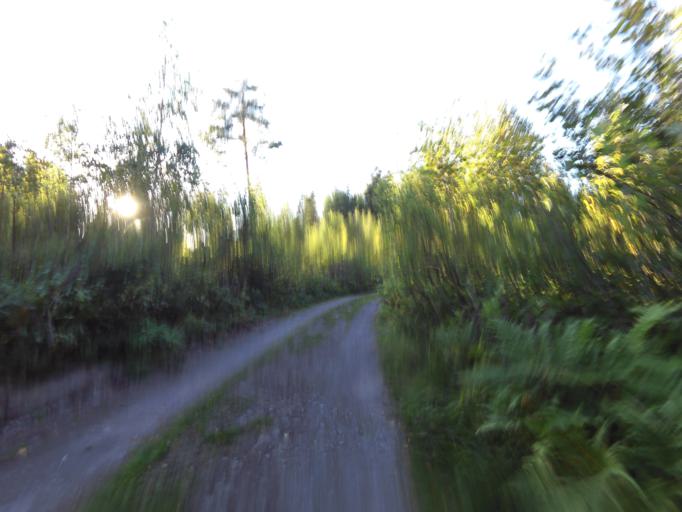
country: SE
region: Gaevleborg
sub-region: Gavle Kommun
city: Gavle
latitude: 60.7210
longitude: 17.1482
